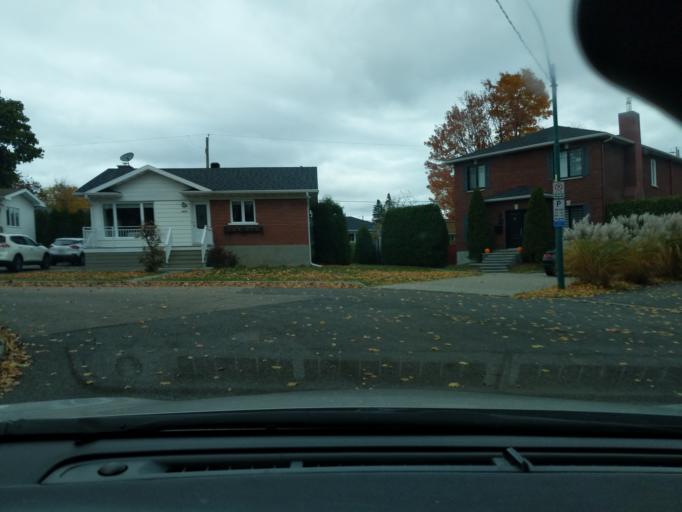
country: CA
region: Quebec
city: Quebec
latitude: 46.7677
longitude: -71.2739
